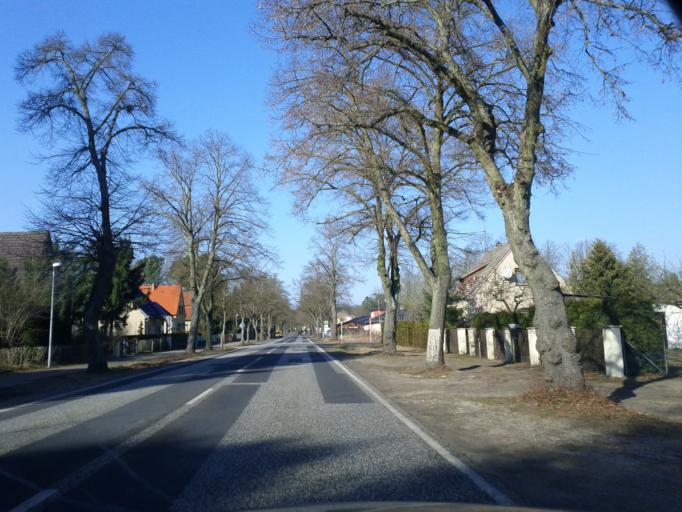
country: DE
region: Brandenburg
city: Spreenhagen
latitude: 52.3914
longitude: 13.9433
